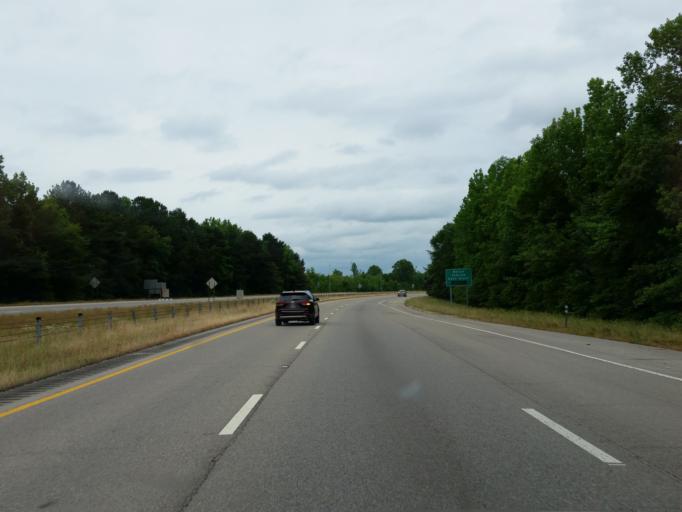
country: US
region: Alabama
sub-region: Sumter County
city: York
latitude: 32.4294
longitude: -88.4493
